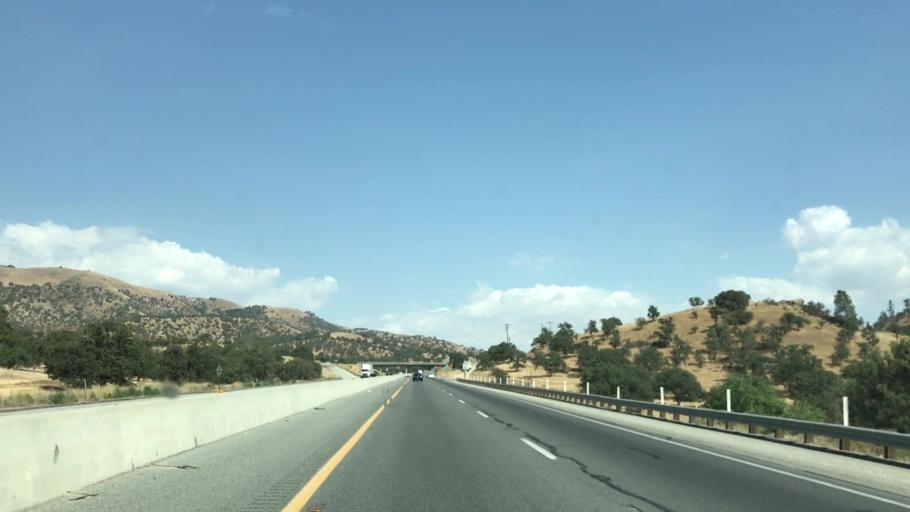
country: US
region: California
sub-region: Kern County
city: Golden Hills
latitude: 35.2022
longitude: -118.5270
